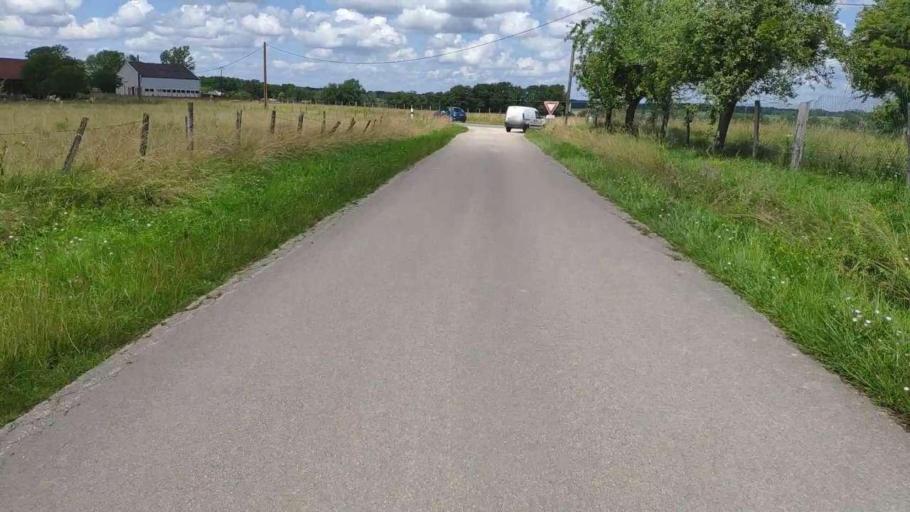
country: FR
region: Franche-Comte
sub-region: Departement du Jura
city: Bletterans
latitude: 46.8423
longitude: 5.4893
